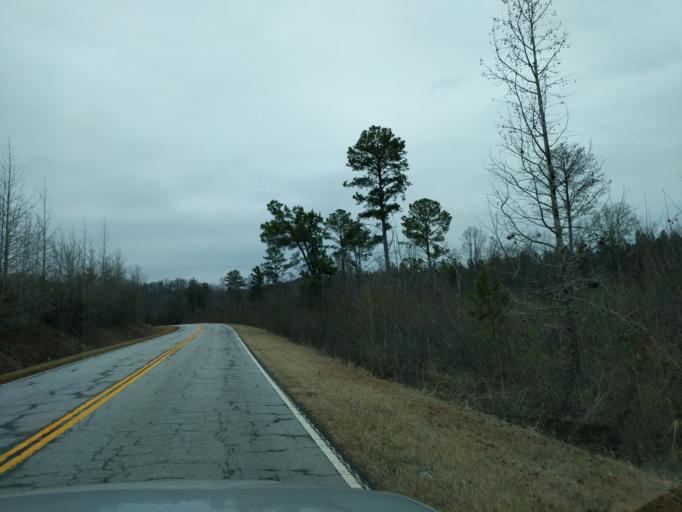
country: US
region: South Carolina
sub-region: Oconee County
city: Walhalla
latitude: 34.7877
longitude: -83.1152
